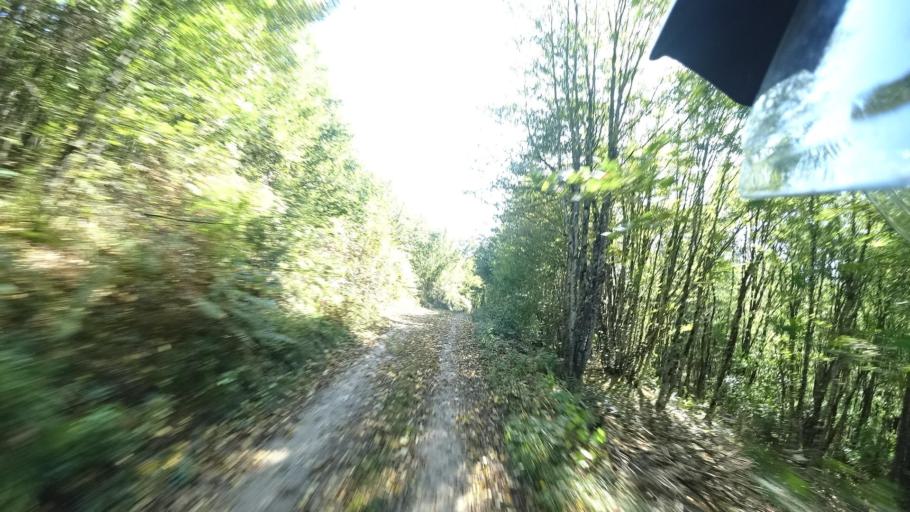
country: HR
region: Karlovacka
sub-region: Grad Ogulin
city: Ogulin
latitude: 45.2032
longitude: 15.1235
